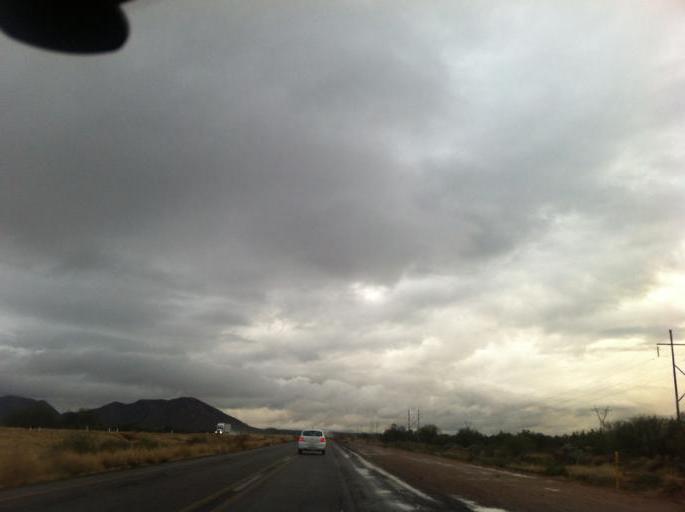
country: MX
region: Sonora
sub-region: San Miguel de Horcasitas
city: Las Mercedes [Agropecuaria]
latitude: 29.5654
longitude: -111.0160
